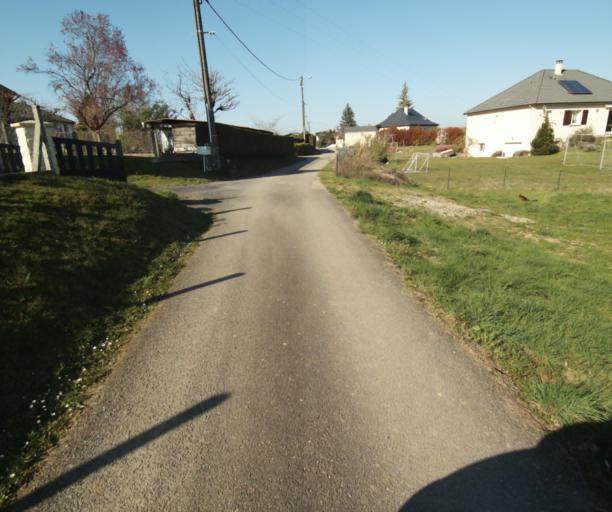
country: FR
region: Limousin
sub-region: Departement de la Correze
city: Saint-Mexant
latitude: 45.2948
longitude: 1.6904
